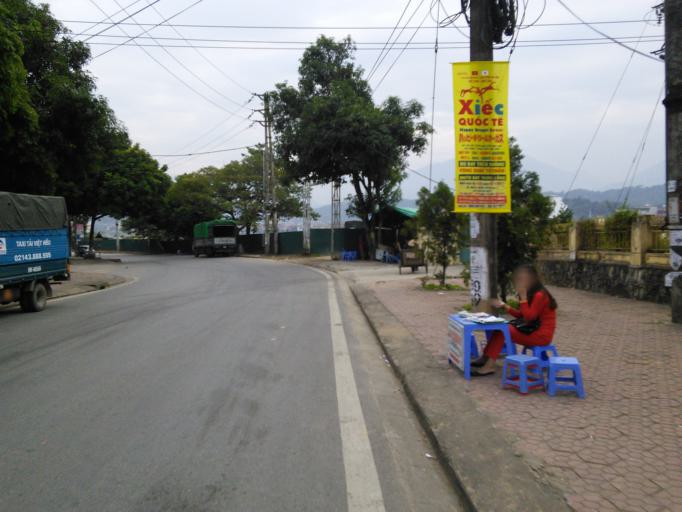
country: VN
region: Lao Cai
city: Lao Cai
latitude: 22.4974
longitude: 103.9723
